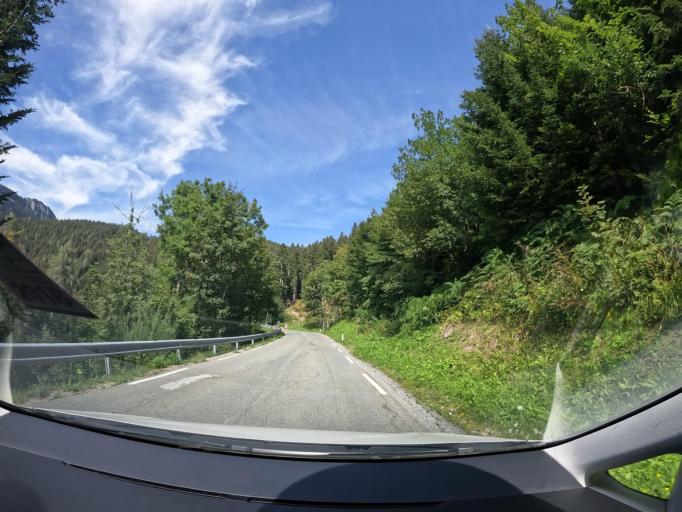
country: AT
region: Carinthia
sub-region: Politischer Bezirk Sankt Veit an der Glan
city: Liebenfels
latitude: 46.7142
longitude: 14.2573
